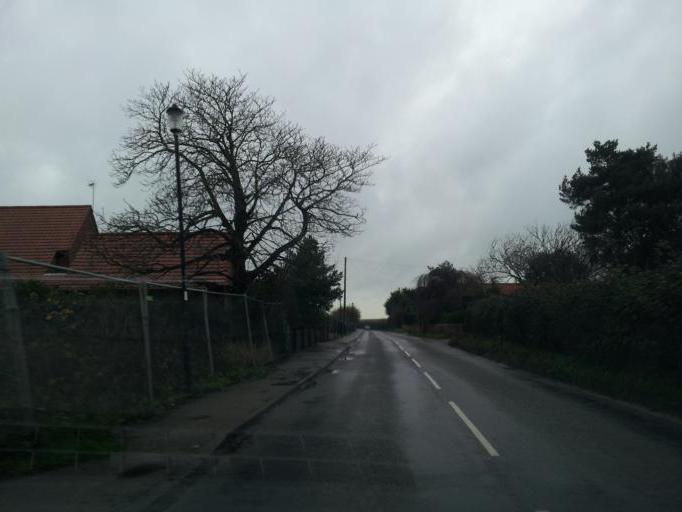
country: GB
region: England
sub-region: Norfolk
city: Hemsby
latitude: 52.6996
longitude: 1.6794
